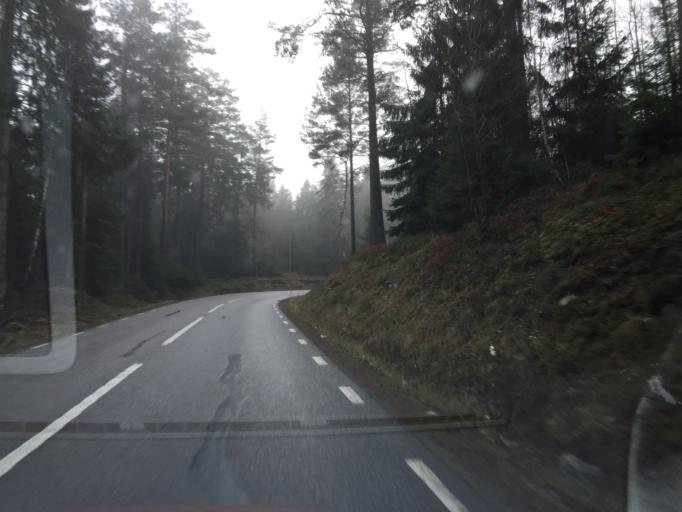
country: SE
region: Stockholm
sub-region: Botkyrka Kommun
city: Varsta
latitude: 59.1290
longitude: 17.8451
